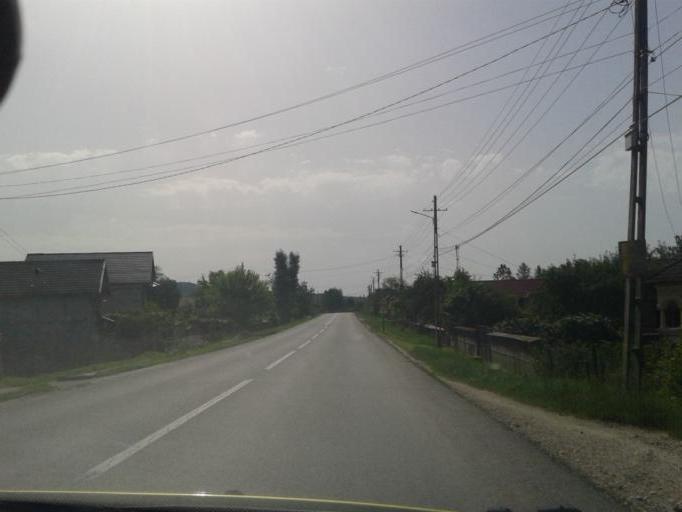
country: RO
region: Valcea
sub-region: Comuna Bunesti
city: Bunesti
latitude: 45.1100
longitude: 24.1852
